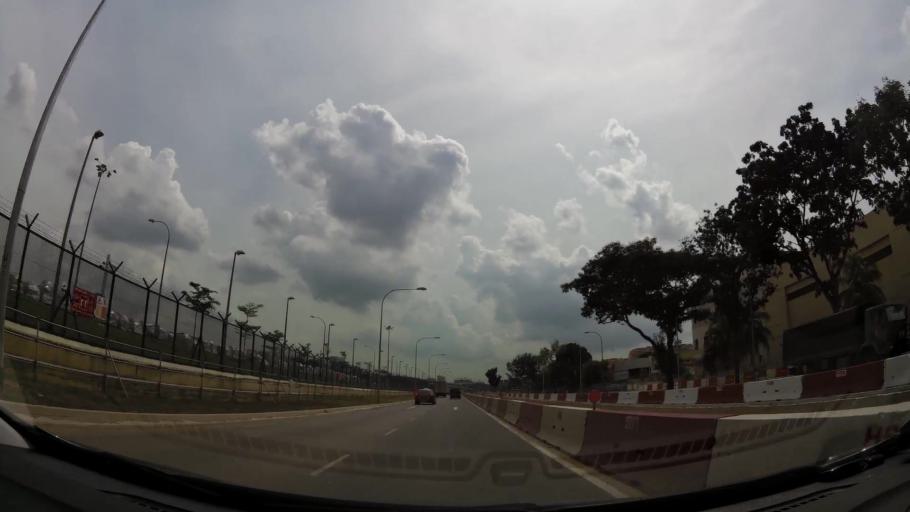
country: MY
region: Johor
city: Johor Bahru
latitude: 1.4020
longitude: 103.7560
